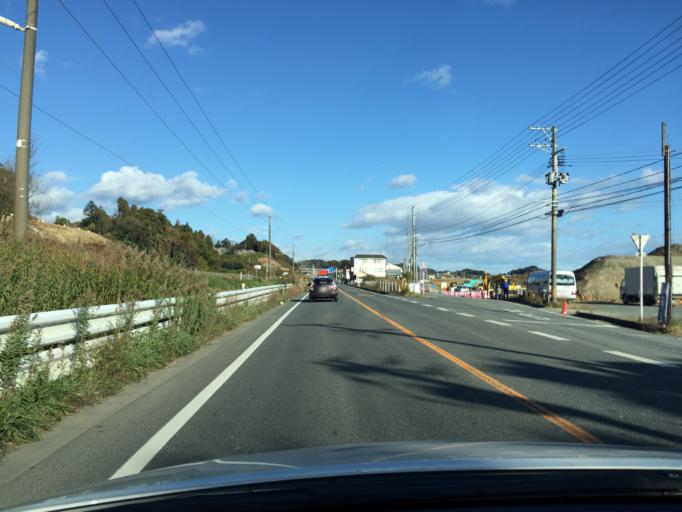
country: JP
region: Fukushima
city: Iwaki
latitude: 37.1322
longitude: 140.9970
